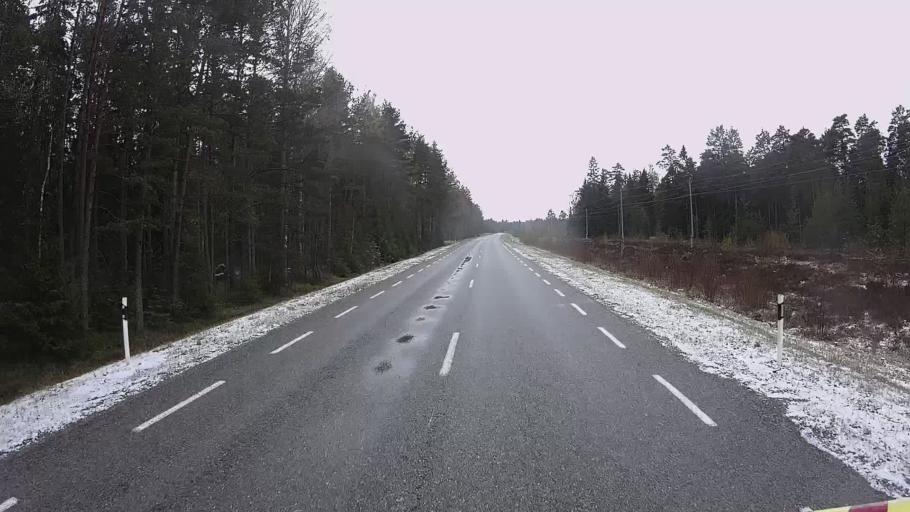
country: EE
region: Hiiumaa
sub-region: Kaerdla linn
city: Kardla
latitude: 59.0193
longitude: 22.6719
